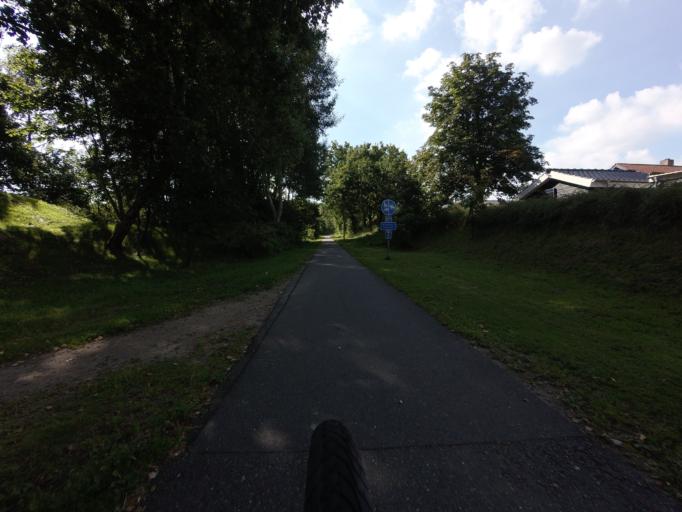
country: DK
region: Central Jutland
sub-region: Viborg Kommune
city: Viborg
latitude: 56.4106
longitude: 9.3617
